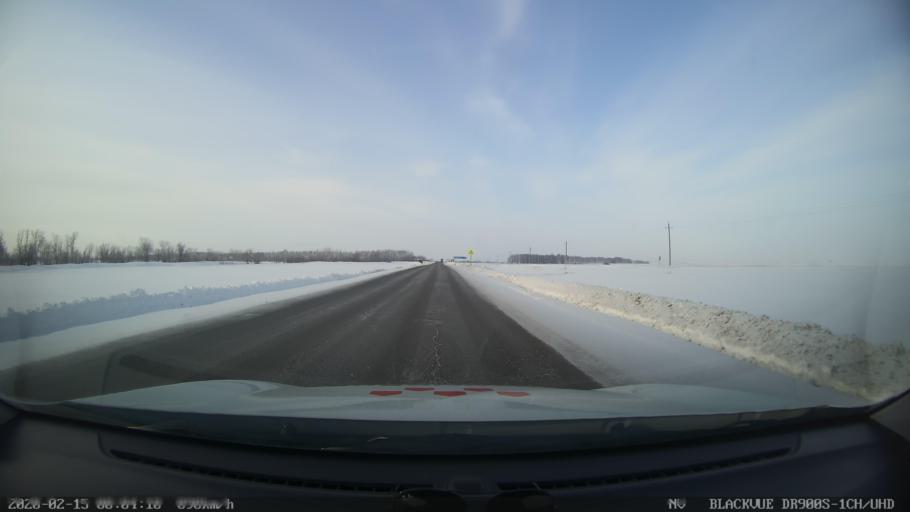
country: RU
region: Tatarstan
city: Kuybyshevskiy Zaton
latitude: 55.3795
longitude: 48.9874
